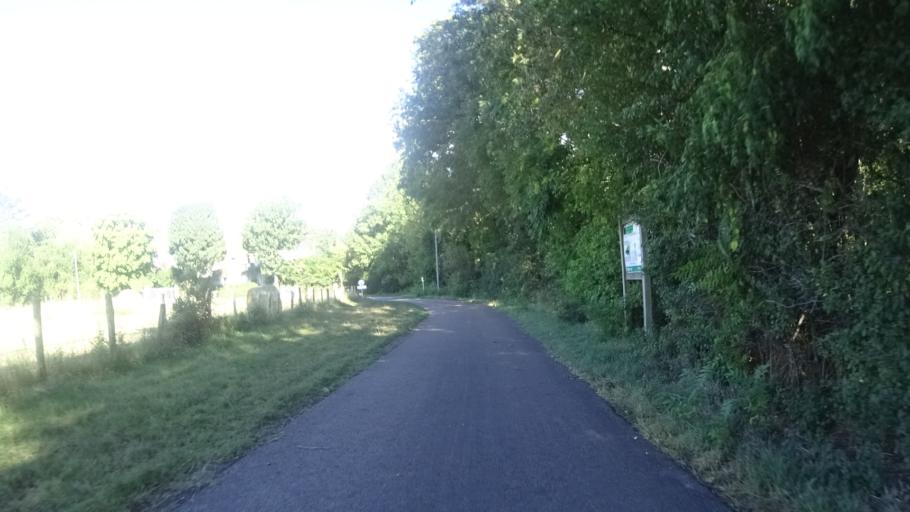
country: FR
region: Centre
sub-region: Departement du Cher
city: Sancerre
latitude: 47.3104
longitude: 2.8905
